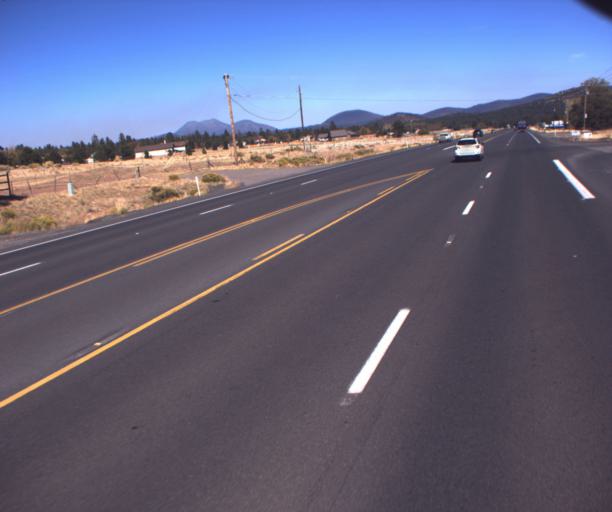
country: US
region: Arizona
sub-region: Coconino County
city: Flagstaff
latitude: 35.2545
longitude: -111.5556
